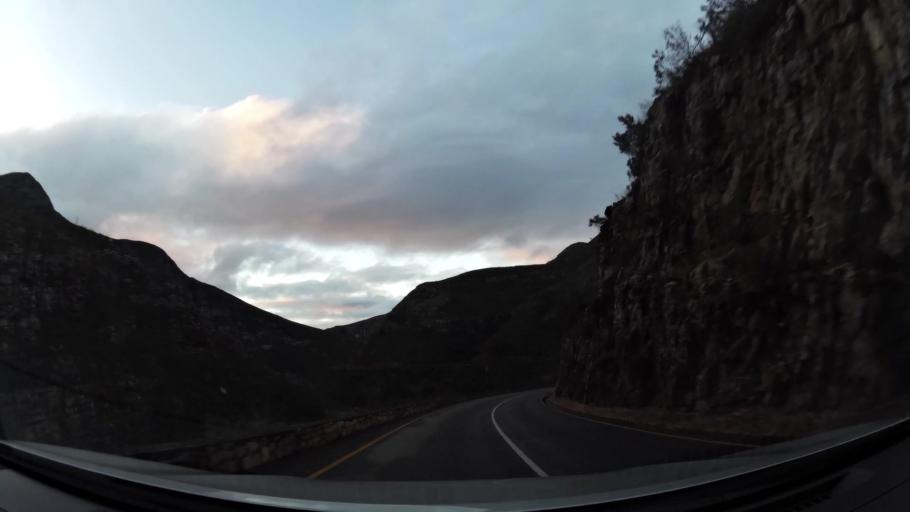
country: ZA
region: Western Cape
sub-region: Overberg District Municipality
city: Swellendam
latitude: -33.9701
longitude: 20.7017
